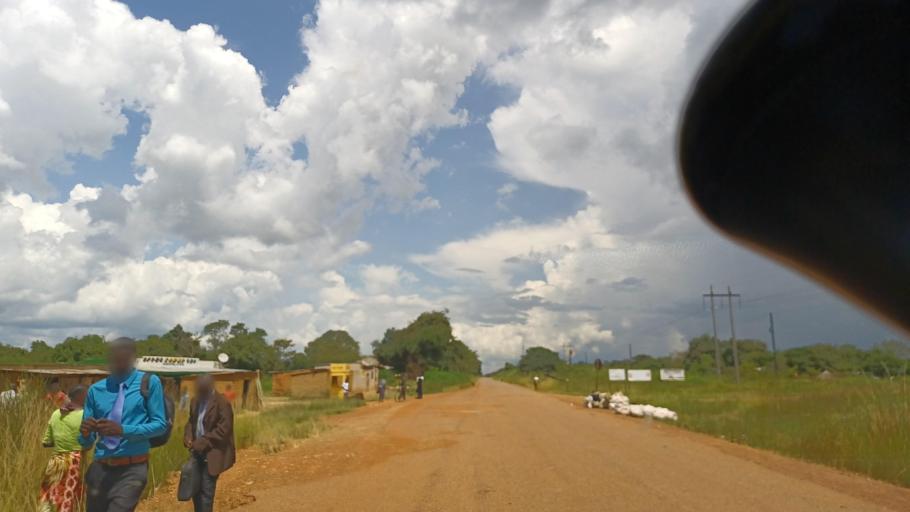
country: ZM
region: North-Western
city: Kasempa
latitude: -12.7854
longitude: 26.0111
